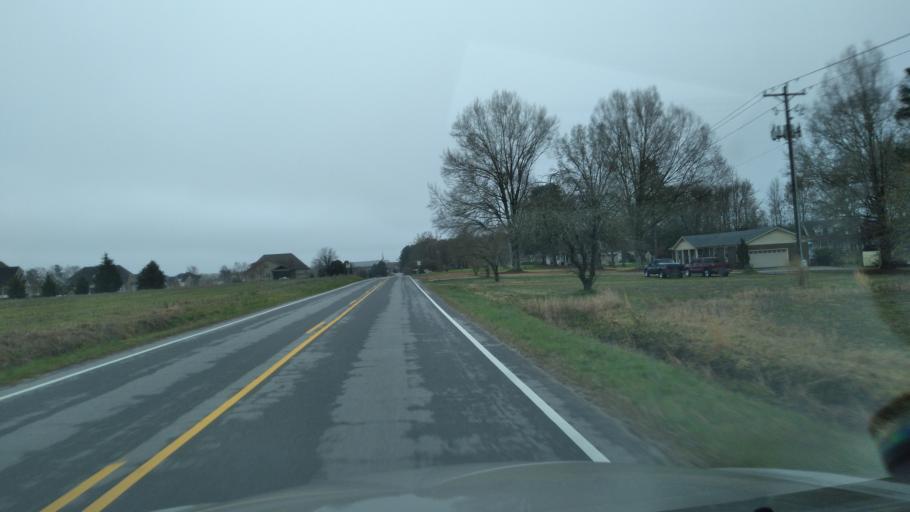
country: US
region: North Carolina
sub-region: Wake County
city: Knightdale
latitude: 35.7564
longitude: -78.4838
